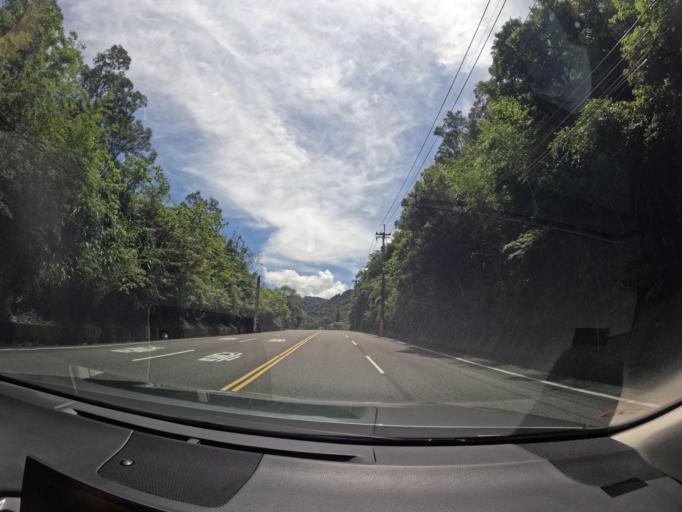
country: TW
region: Taiwan
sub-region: Miaoli
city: Miaoli
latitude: 24.4777
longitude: 120.8911
